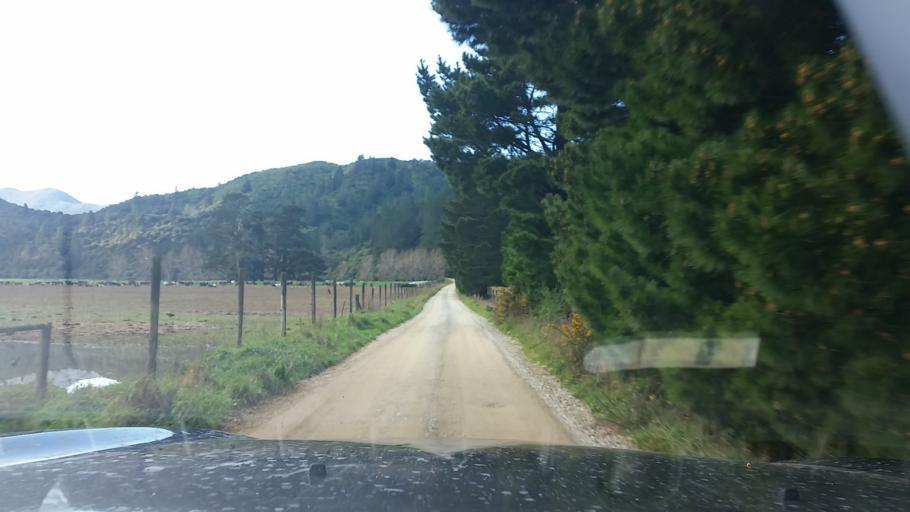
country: NZ
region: Marlborough
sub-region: Marlborough District
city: Picton
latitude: -41.1431
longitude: 174.1373
